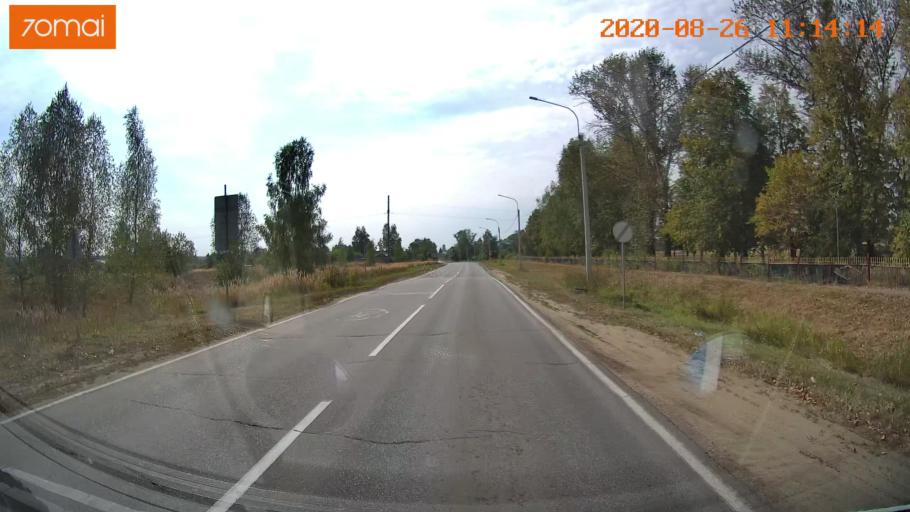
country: RU
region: Rjazan
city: Izhevskoye
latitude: 54.4507
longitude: 41.1176
